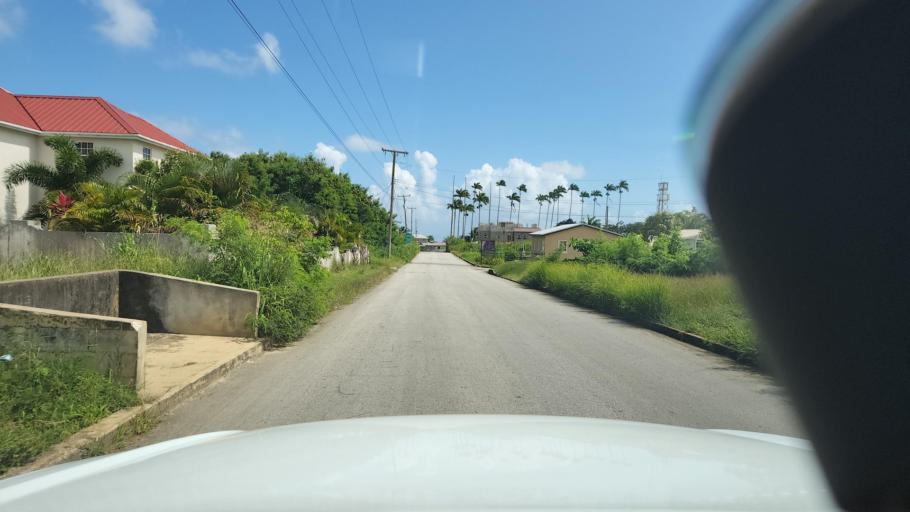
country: BB
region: Saint John
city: Four Cross Roads
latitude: 13.1833
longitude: -59.5008
